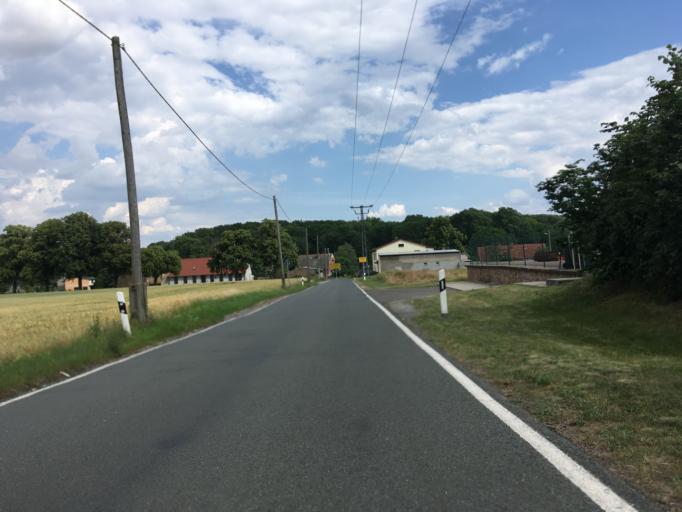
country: DE
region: Saxony-Anhalt
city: Baalberge
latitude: 51.7706
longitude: 11.8557
